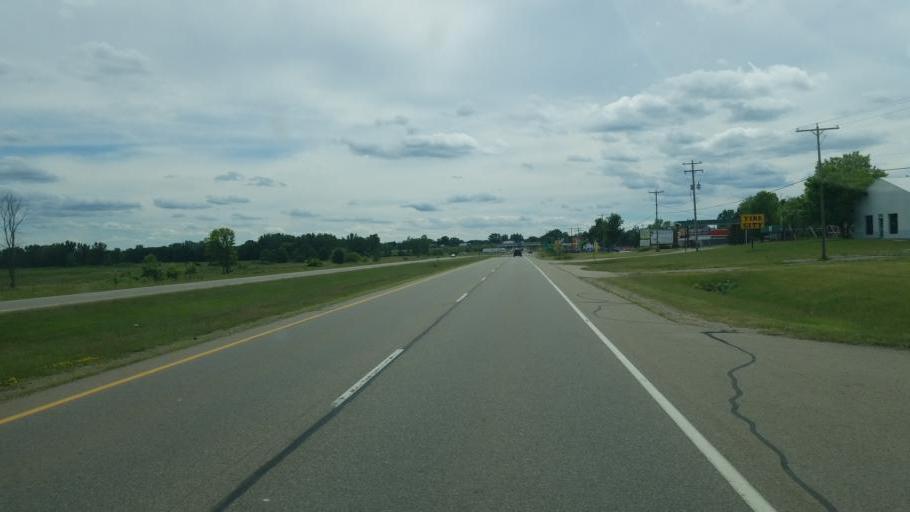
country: US
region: Michigan
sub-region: Eaton County
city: Charlotte
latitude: 42.5799
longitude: -84.8119
